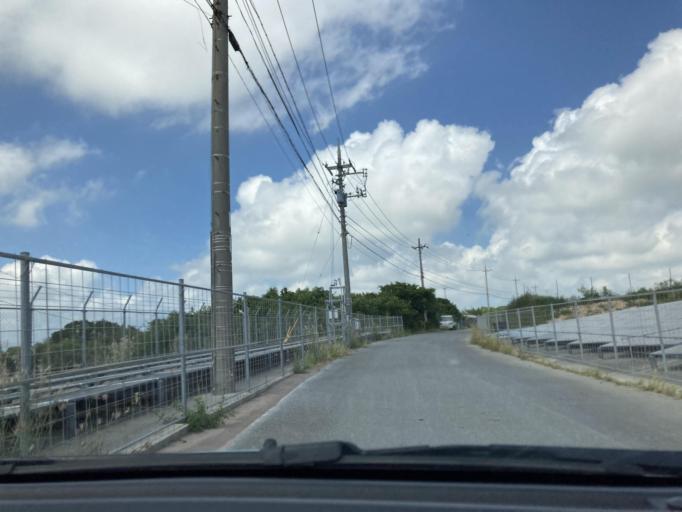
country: JP
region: Okinawa
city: Itoman
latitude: 26.1008
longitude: 127.7281
